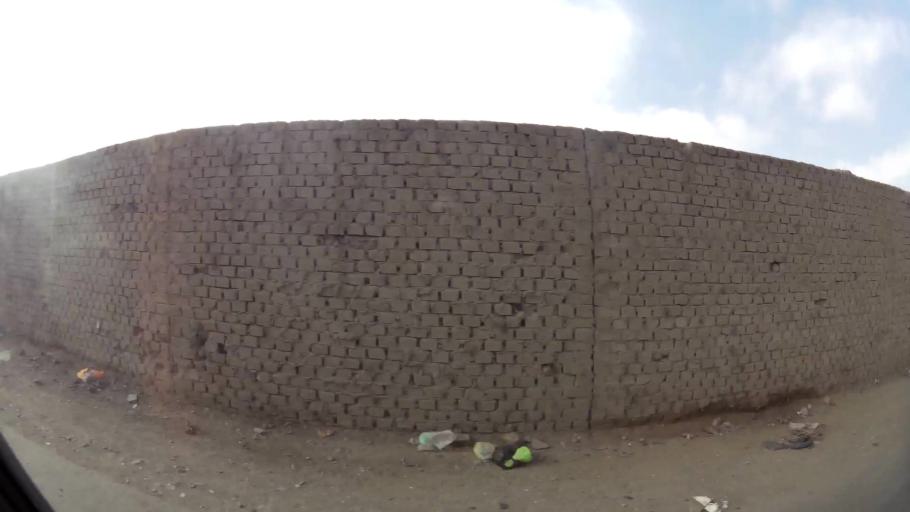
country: PE
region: La Libertad
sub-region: Provincia de Trujillo
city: Trujillo
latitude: -8.0935
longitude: -79.0290
